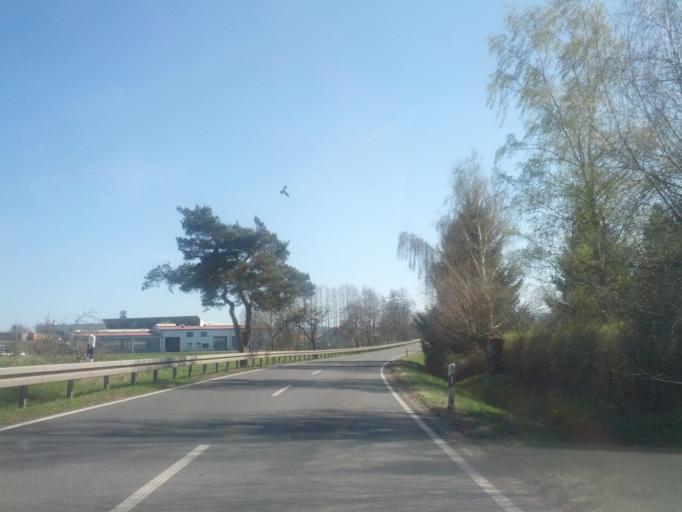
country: DE
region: Thuringia
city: Waltershausen
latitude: 50.9251
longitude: 10.5487
